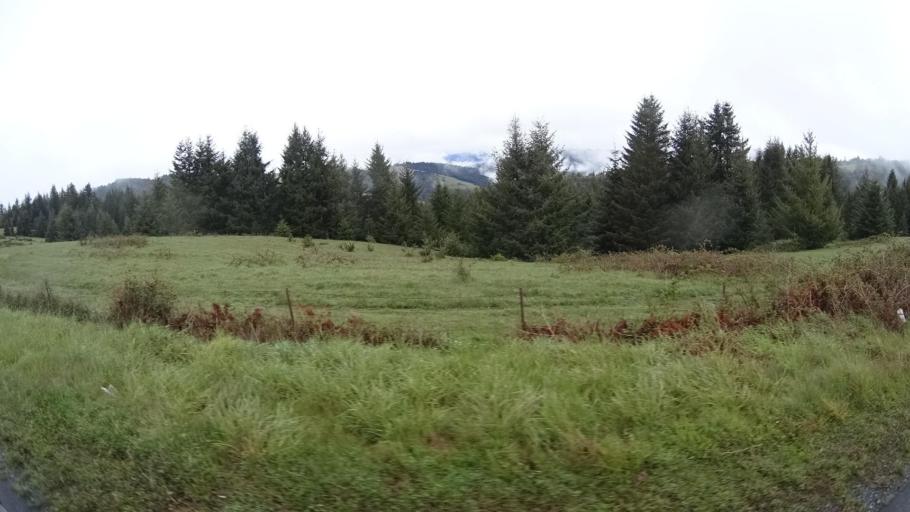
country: US
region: California
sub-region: Humboldt County
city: Westhaven-Moonstone
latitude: 41.1646
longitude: -123.9080
